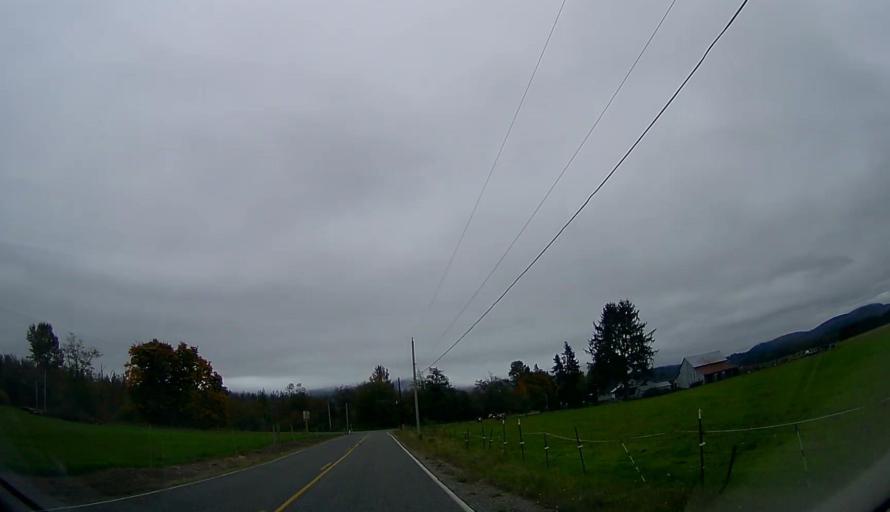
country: US
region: Washington
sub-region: Skagit County
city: Sedro-Woolley
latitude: 48.5165
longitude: -122.1399
